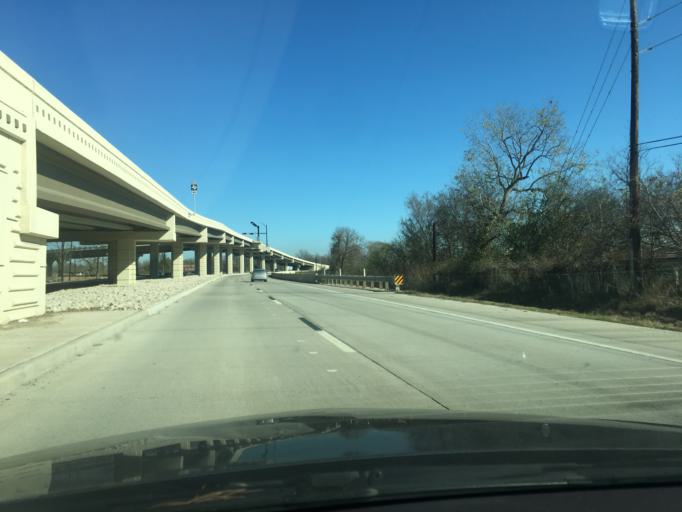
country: US
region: Texas
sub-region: Fort Bend County
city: Richmond
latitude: 29.5928
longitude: -95.7438
